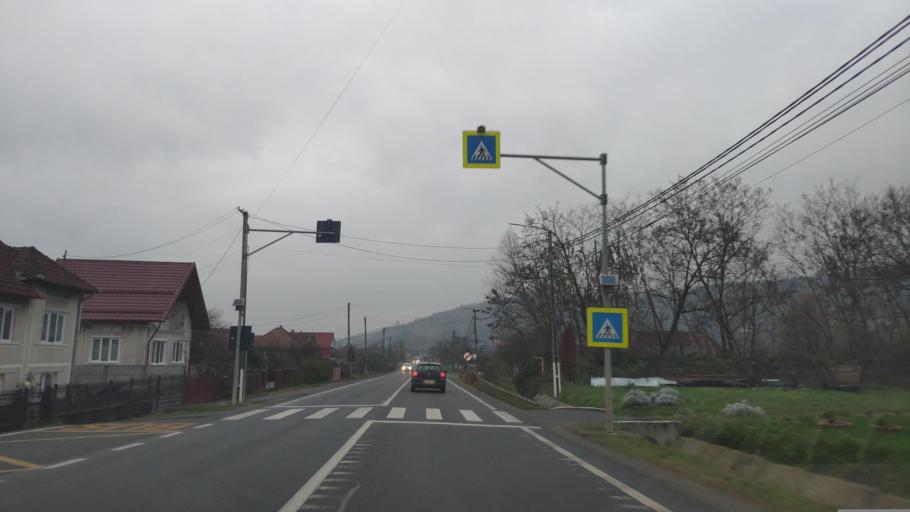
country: RO
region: Maramures
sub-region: Comuna Cicarlau
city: Ilba
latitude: 47.7097
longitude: 23.3662
